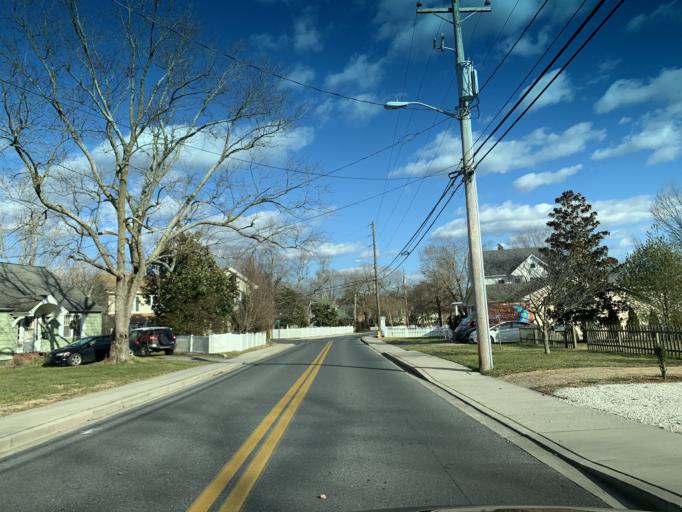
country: US
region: Maryland
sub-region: Worcester County
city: Berlin
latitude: 38.3244
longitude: -75.2161
